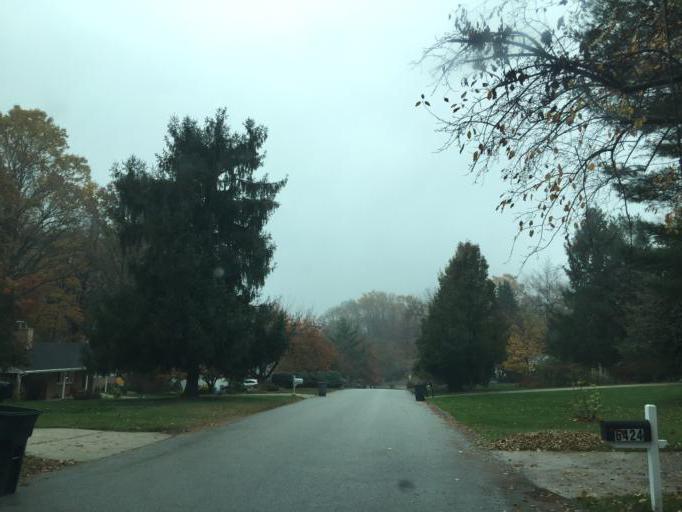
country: US
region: Maryland
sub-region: Howard County
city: Riverside
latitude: 39.1945
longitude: -76.8618
